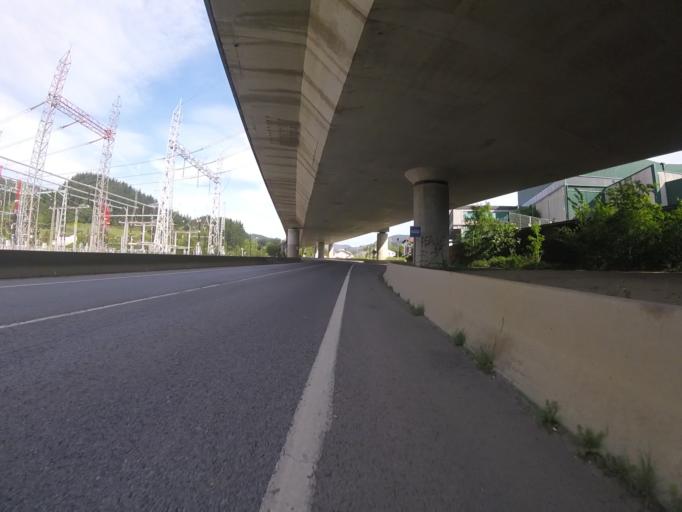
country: ES
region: Basque Country
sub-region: Provincia de Guipuzcoa
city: Gabiria
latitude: 43.0623
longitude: -2.2736
